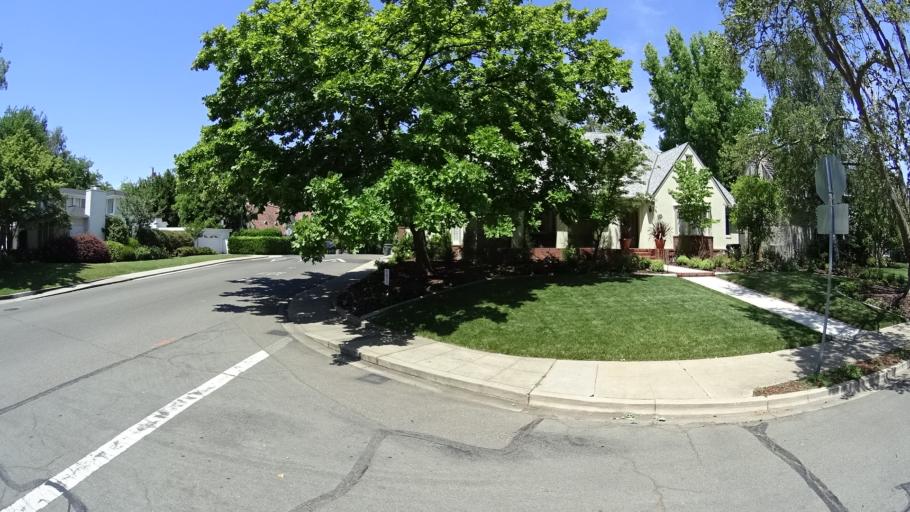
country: US
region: California
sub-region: Sacramento County
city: Sacramento
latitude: 38.5651
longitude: -121.4473
